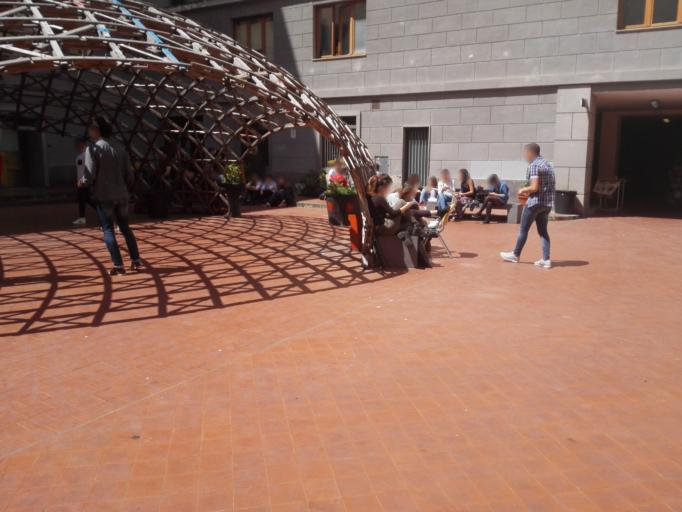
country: IT
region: Campania
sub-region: Provincia di Napoli
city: Napoli
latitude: 40.8468
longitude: 14.2484
